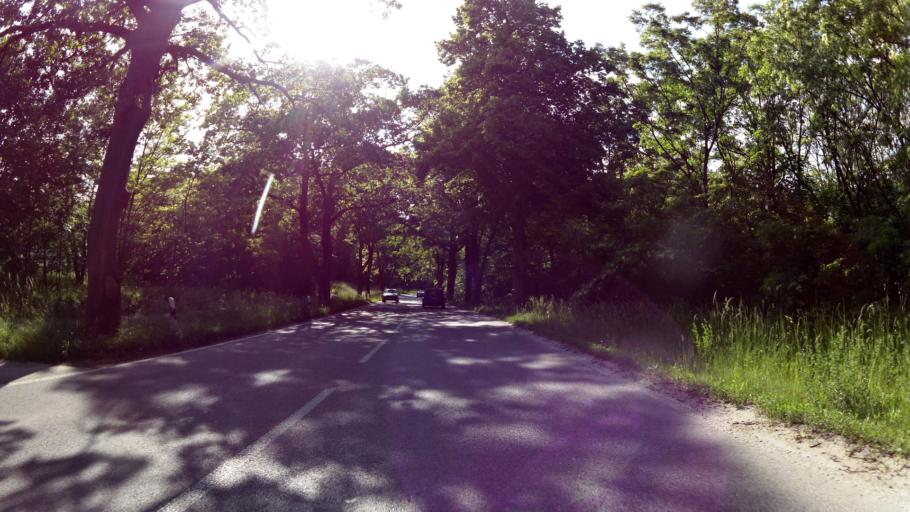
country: DE
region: Brandenburg
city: Petershagen
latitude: 52.4862
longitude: 13.8243
